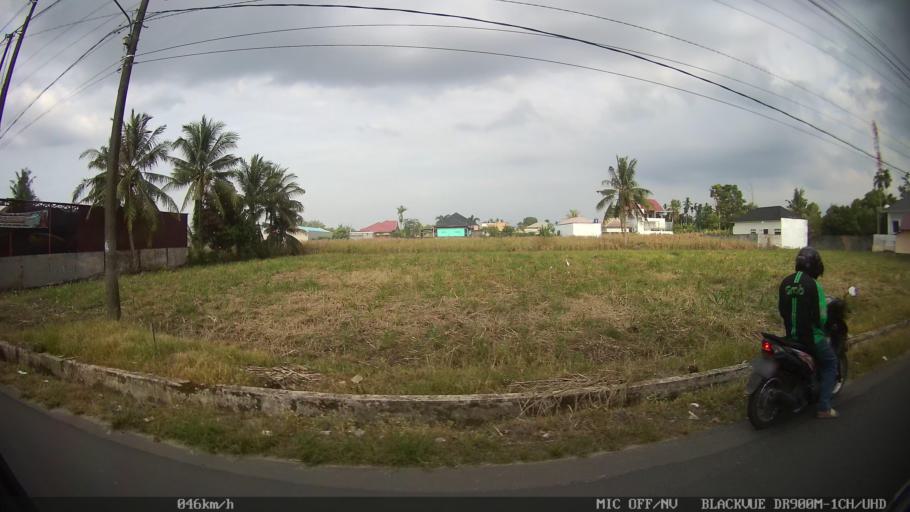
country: ID
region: North Sumatra
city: Sunggal
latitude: 3.5326
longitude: 98.6052
